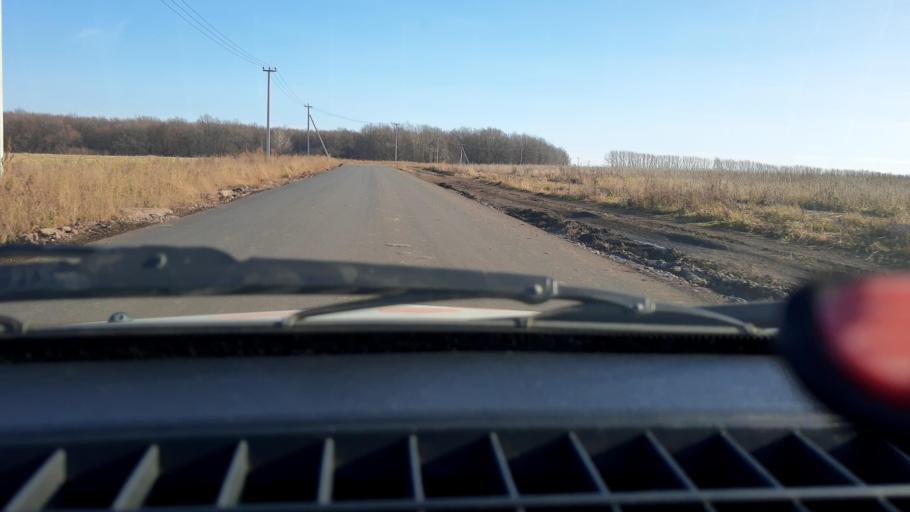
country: RU
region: Bashkortostan
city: Kabakovo
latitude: 54.6234
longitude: 56.1497
